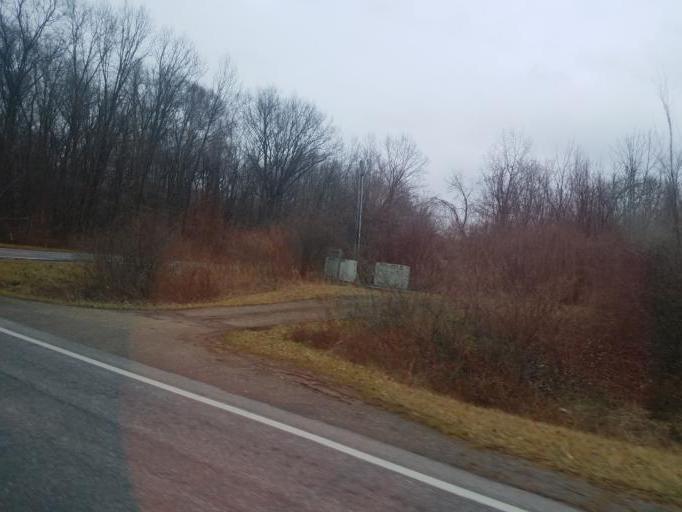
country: US
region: Ohio
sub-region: Delaware County
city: Lewis Center
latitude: 40.1951
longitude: -82.9435
